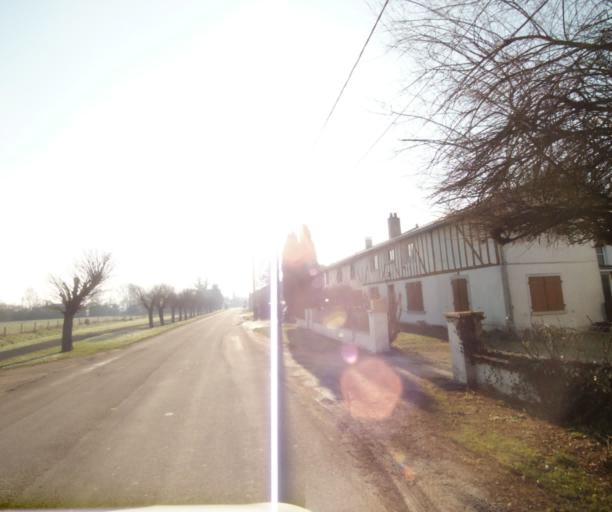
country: FR
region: Champagne-Ardenne
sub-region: Departement de la Haute-Marne
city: Montier-en-Der
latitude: 48.4751
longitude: 4.7632
